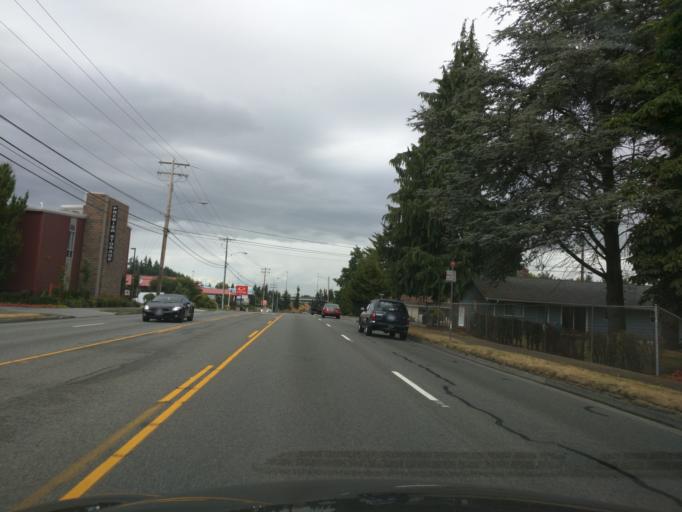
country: US
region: Washington
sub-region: Snohomish County
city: Mill Creek
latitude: 47.9099
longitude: -122.2071
